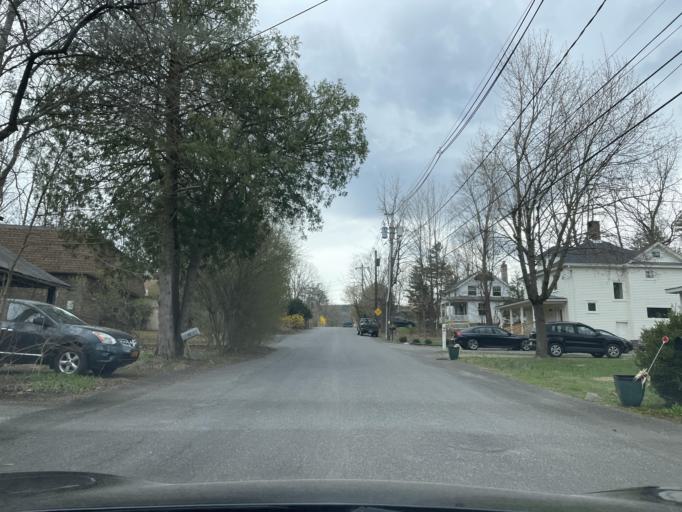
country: US
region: New York
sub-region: Ulster County
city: Woodstock
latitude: 42.0395
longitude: -74.1210
